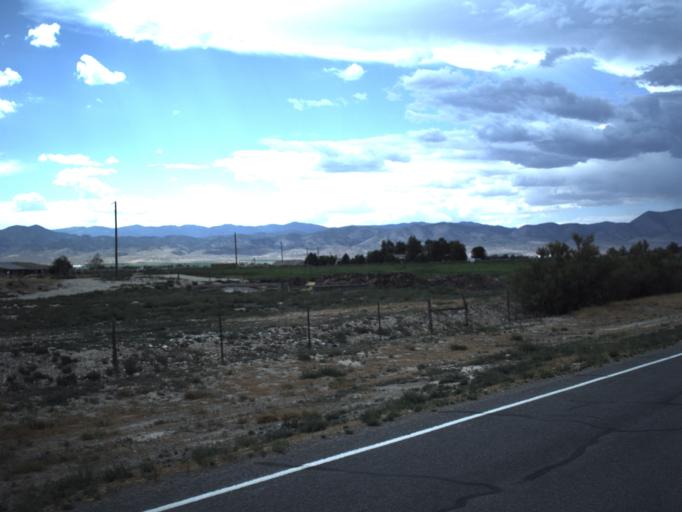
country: US
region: Utah
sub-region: Sanpete County
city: Centerfield
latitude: 39.1384
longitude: -111.7834
